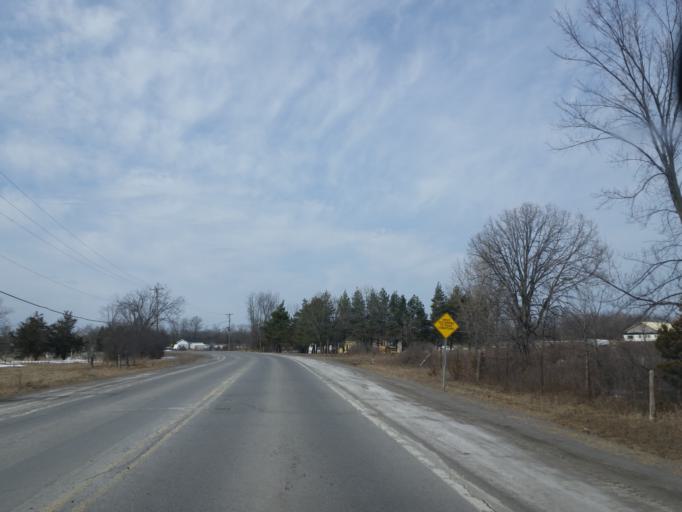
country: CA
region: Ontario
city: Deseronto
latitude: 44.1936
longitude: -77.0935
